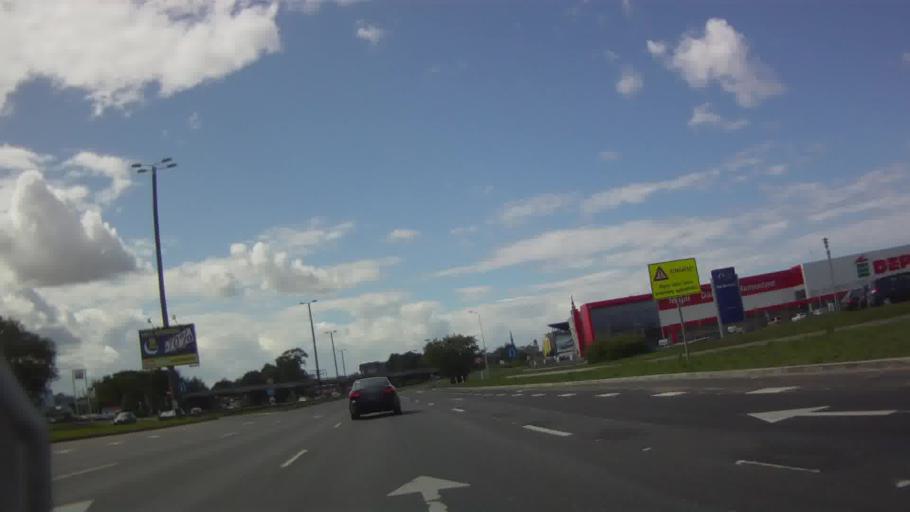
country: LV
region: Riga
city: Riga
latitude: 56.9354
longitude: 24.1377
